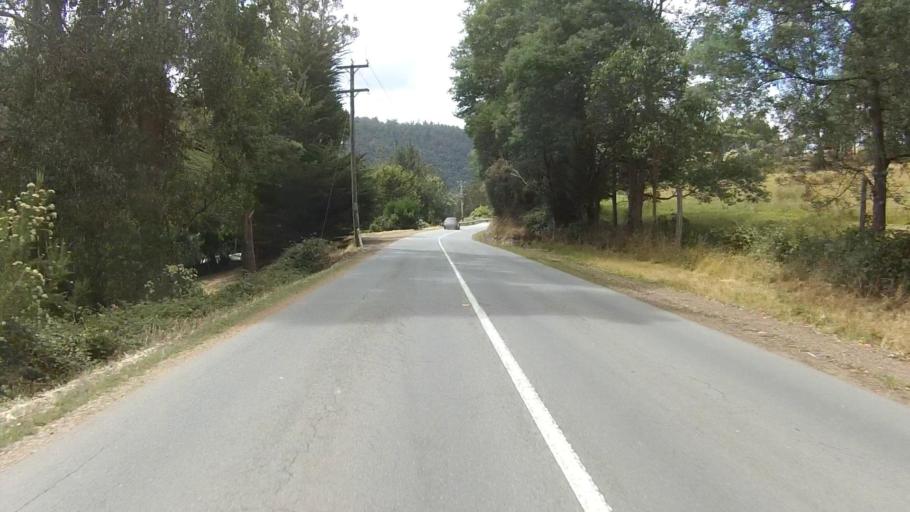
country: AU
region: Tasmania
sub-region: Kingborough
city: Kettering
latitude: -43.1068
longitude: 147.2026
